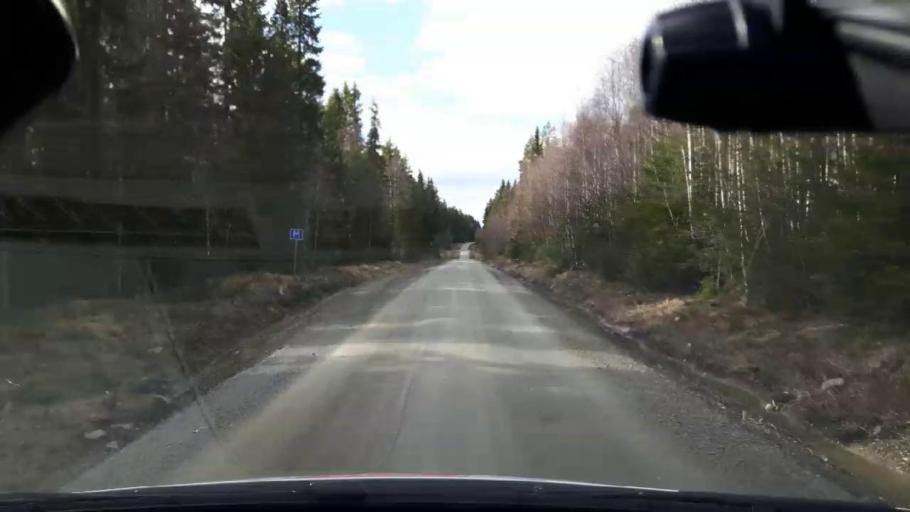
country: SE
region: Jaemtland
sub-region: Bergs Kommun
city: Hoverberg
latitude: 62.9005
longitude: 14.6441
